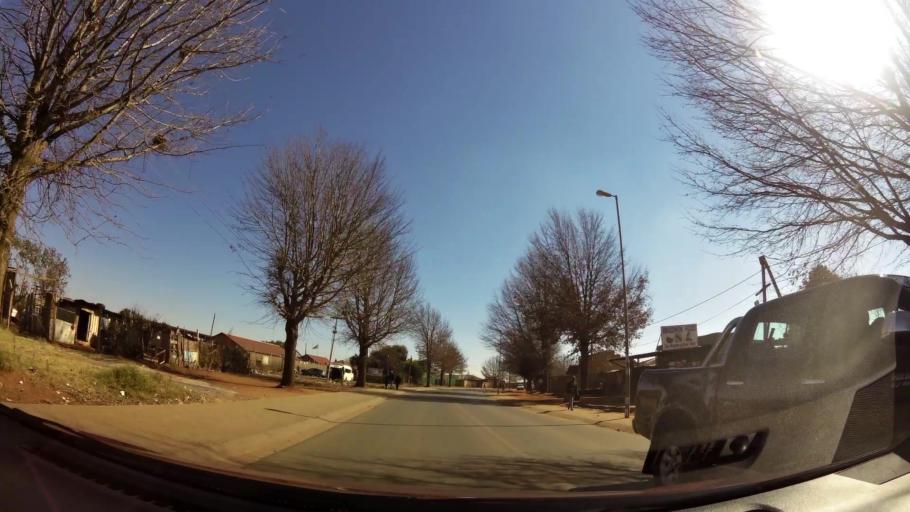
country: ZA
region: Gauteng
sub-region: City of Johannesburg Metropolitan Municipality
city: Soweto
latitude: -26.2204
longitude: 27.8334
